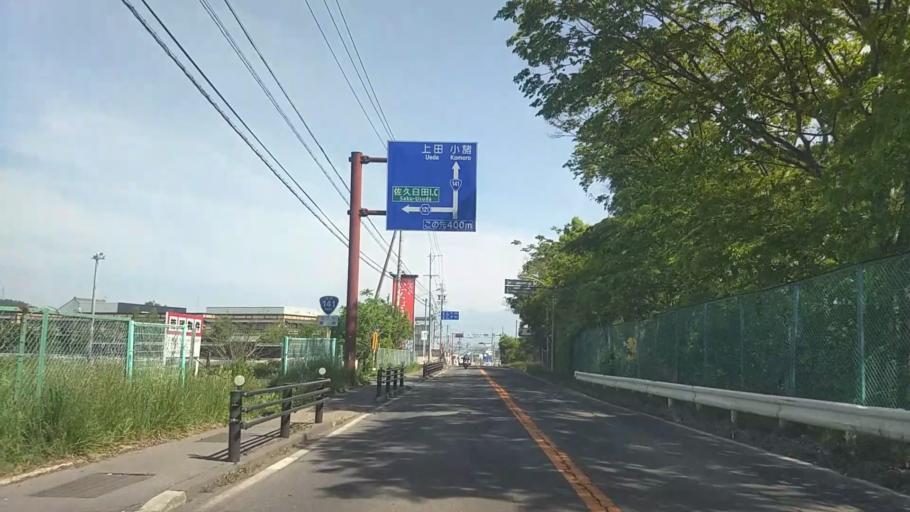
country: JP
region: Nagano
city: Saku
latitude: 36.1870
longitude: 138.4811
